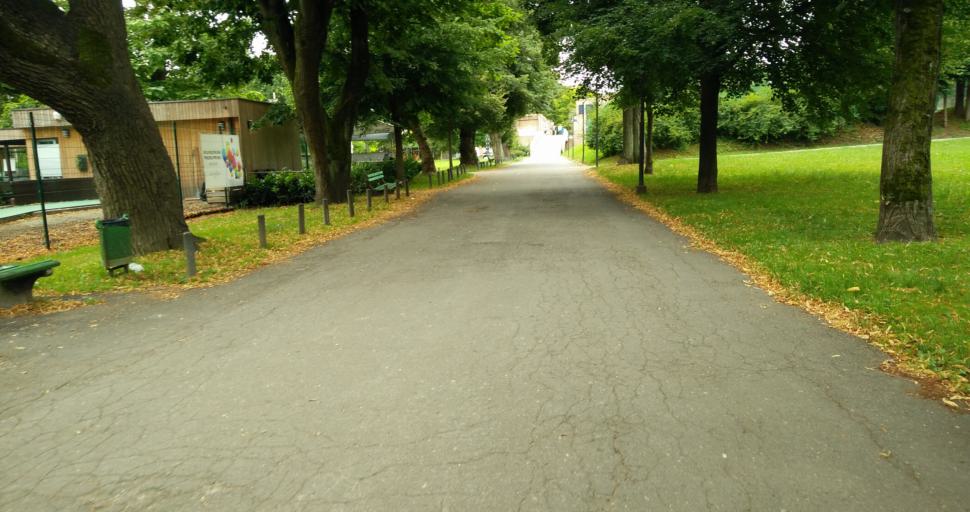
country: SI
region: Ljubljana
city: Ljubljana
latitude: 46.0591
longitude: 14.4969
